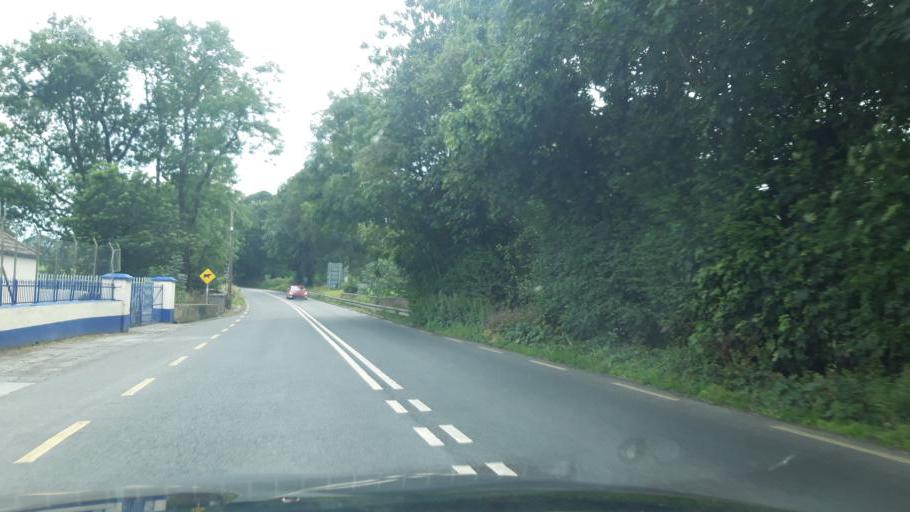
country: IE
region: Leinster
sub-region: Kilkenny
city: Castlecomer
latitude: 52.8458
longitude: -7.1273
